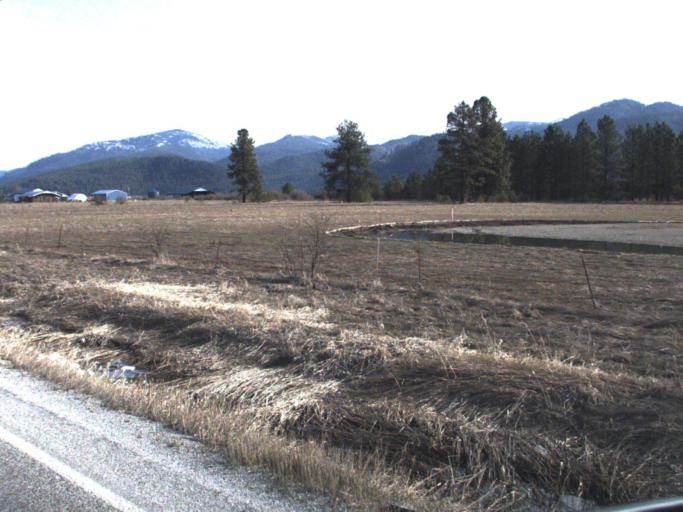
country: US
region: Washington
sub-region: Pend Oreille County
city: Newport
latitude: 48.3503
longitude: -117.3045
